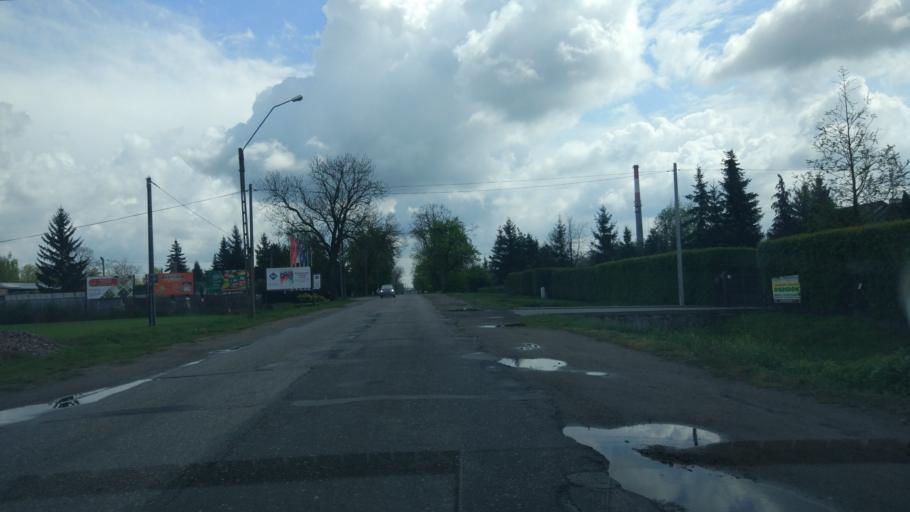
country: PL
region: Lodz Voivodeship
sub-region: Powiat kutnowski
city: Kutno
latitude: 52.2263
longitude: 19.3971
